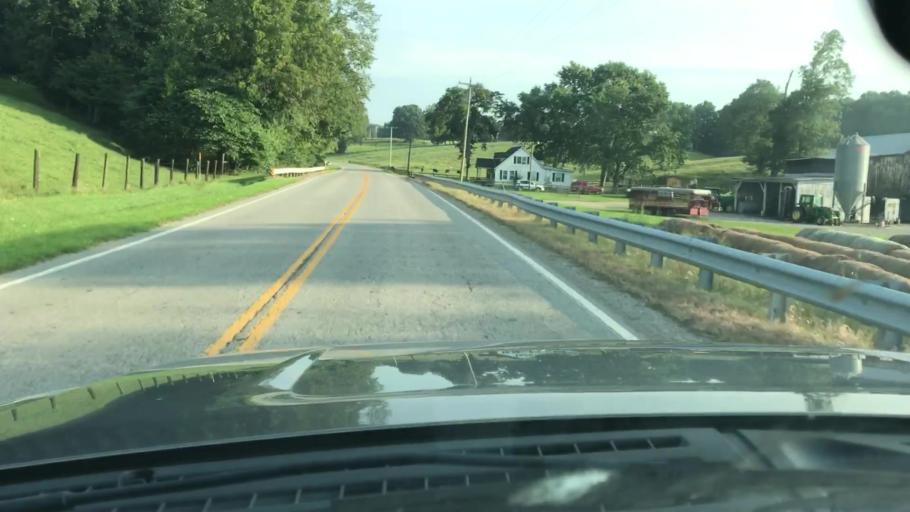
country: US
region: Tennessee
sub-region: Sumner County
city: Portland
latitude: 36.5264
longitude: -86.4255
